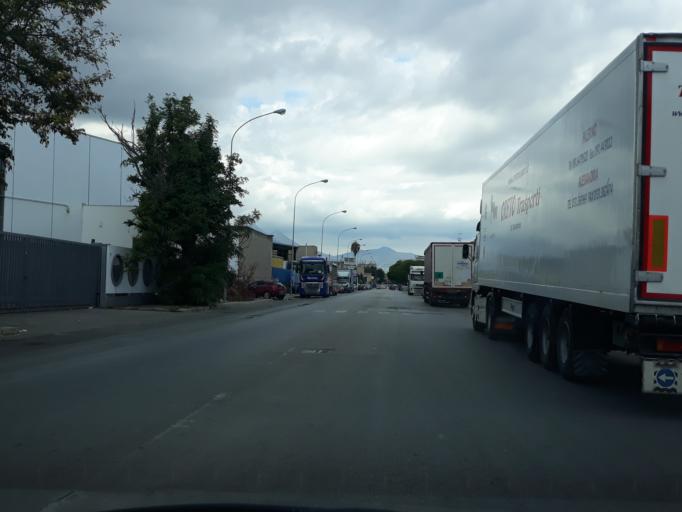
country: IT
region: Sicily
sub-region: Palermo
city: Ciaculli
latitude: 38.0941
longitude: 13.4023
